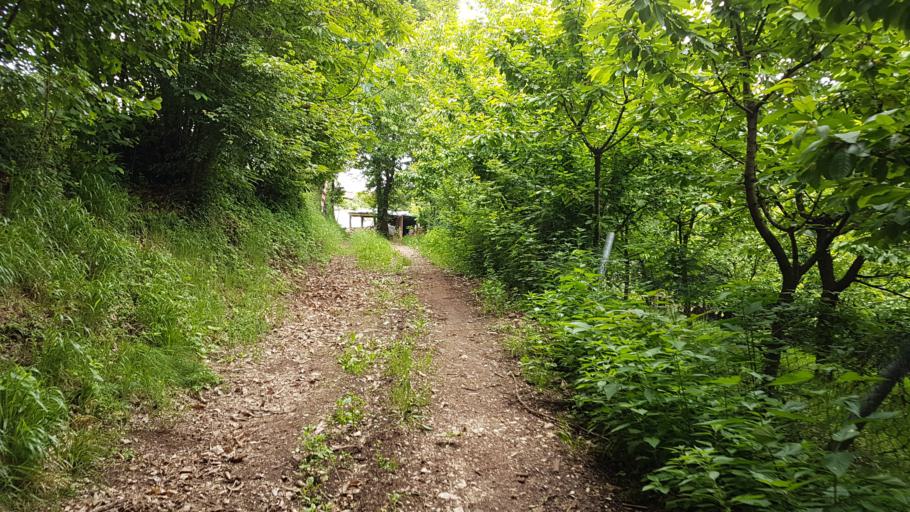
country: IT
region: Veneto
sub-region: Provincia di Vicenza
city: Nogarole Vicentino
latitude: 45.5457
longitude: 11.3216
